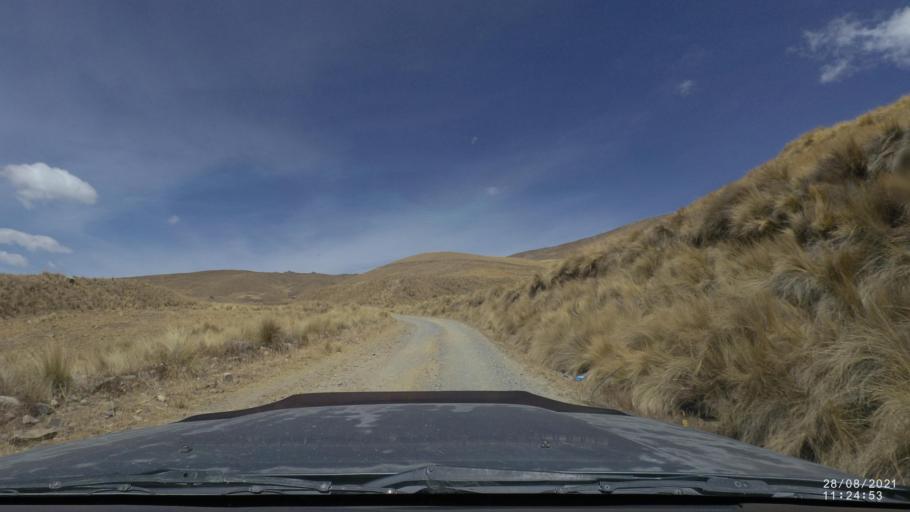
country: BO
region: Cochabamba
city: Sipe Sipe
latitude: -17.1694
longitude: -66.3522
